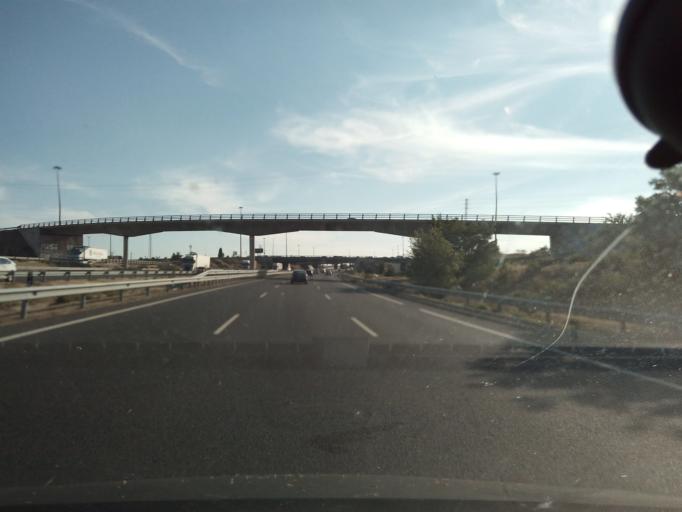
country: ES
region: Madrid
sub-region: Provincia de Madrid
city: Pinto
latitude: 40.2785
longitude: -3.6874
